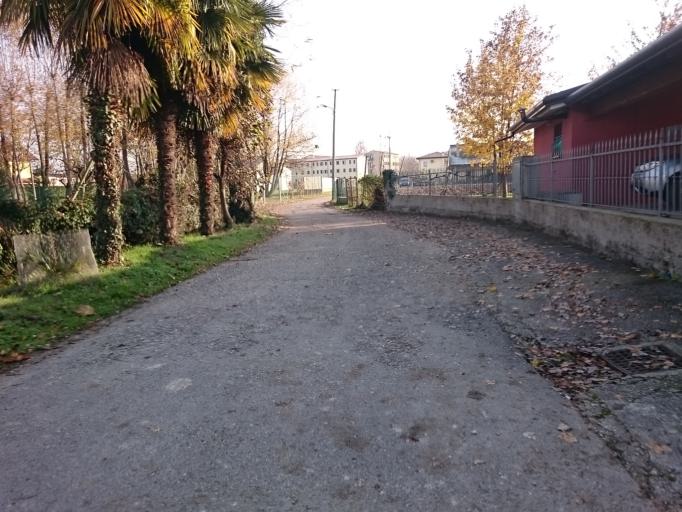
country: IT
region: Veneto
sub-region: Provincia di Padova
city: Ponte San Nicolo
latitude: 45.3729
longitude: 11.9087
